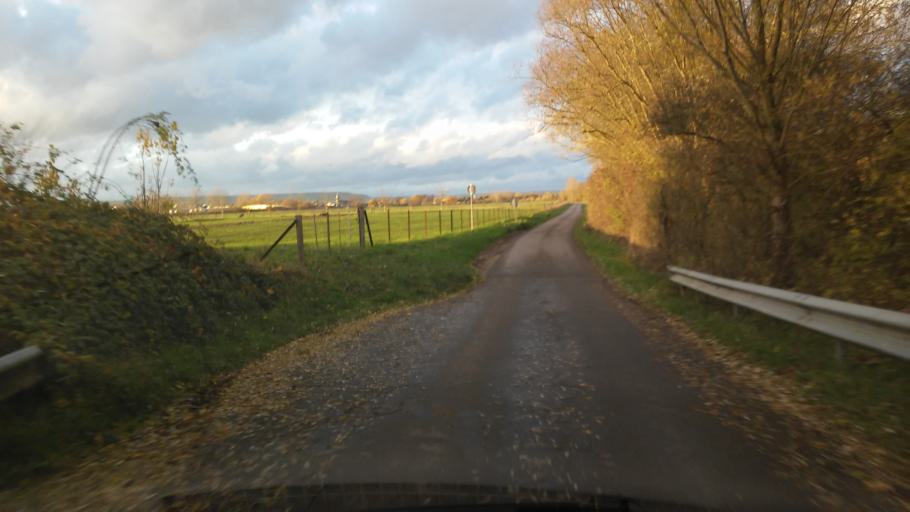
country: FR
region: Lorraine
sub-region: Departement de la Moselle
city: Ay-sur-Moselle
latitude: 49.2250
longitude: 6.1925
